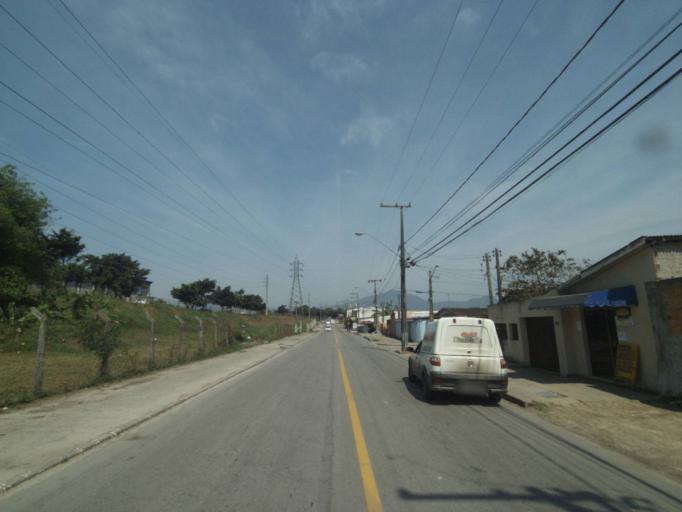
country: BR
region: Parana
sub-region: Paranagua
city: Paranagua
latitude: -25.5432
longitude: -48.5476
